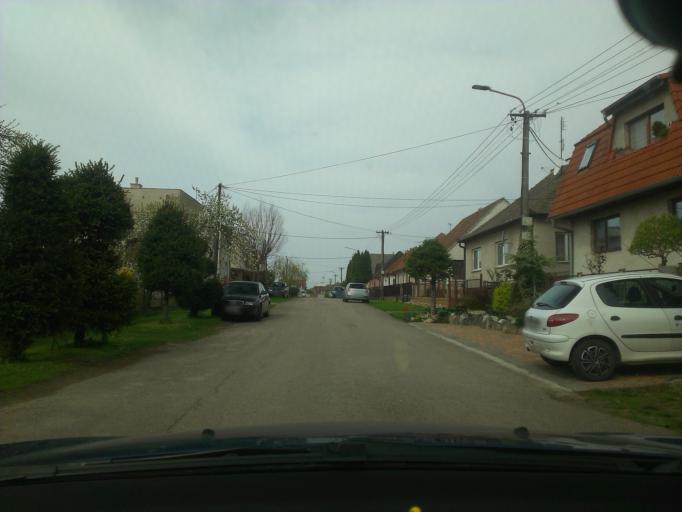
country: SK
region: Trnavsky
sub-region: Okres Trnava
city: Piestany
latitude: 48.5188
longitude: 17.8079
